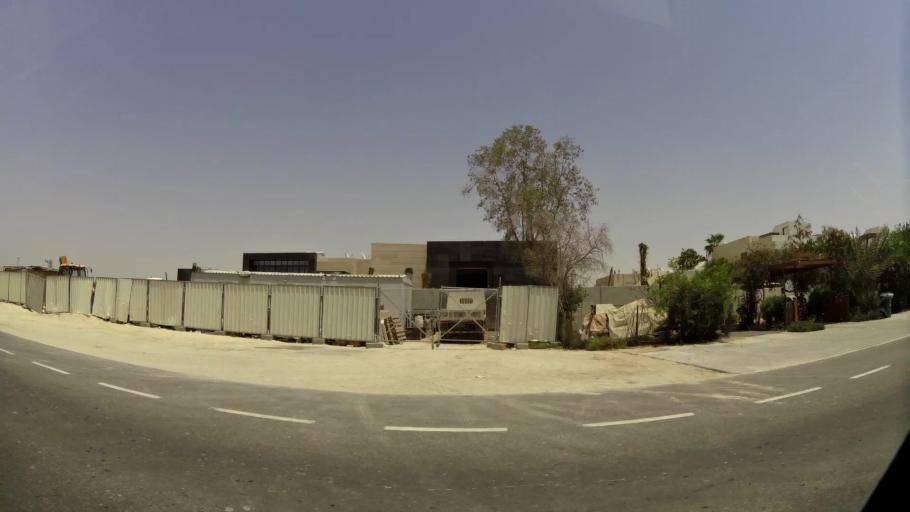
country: AE
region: Dubai
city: Dubai
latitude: 25.1644
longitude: 55.2157
